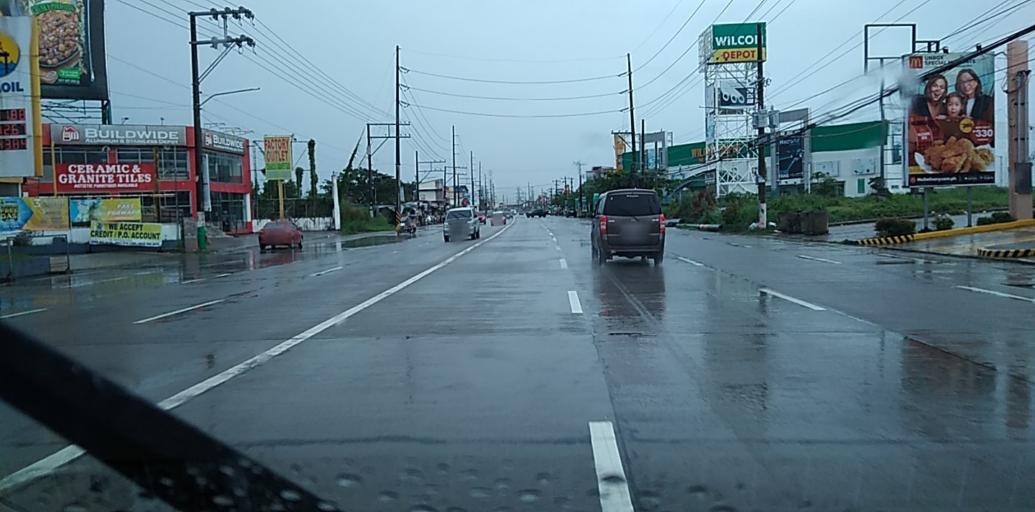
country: PH
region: Central Luzon
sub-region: Province of Pampanga
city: Del Pilar
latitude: 15.0515
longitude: 120.7039
